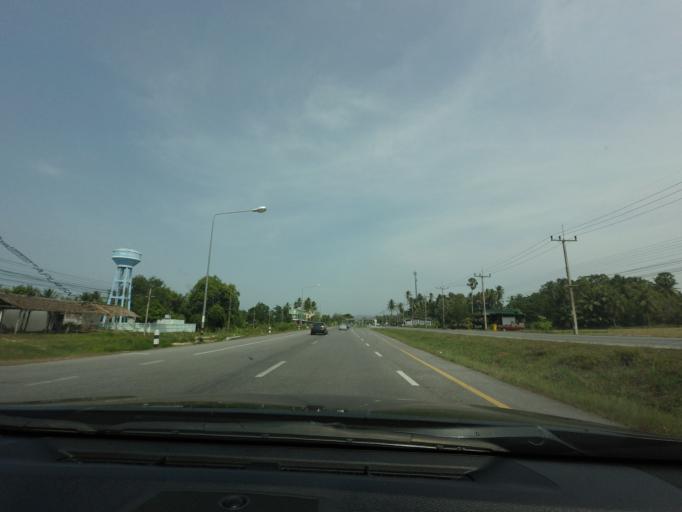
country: TH
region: Pattani
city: Yaring
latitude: 6.8203
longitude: 101.4066
